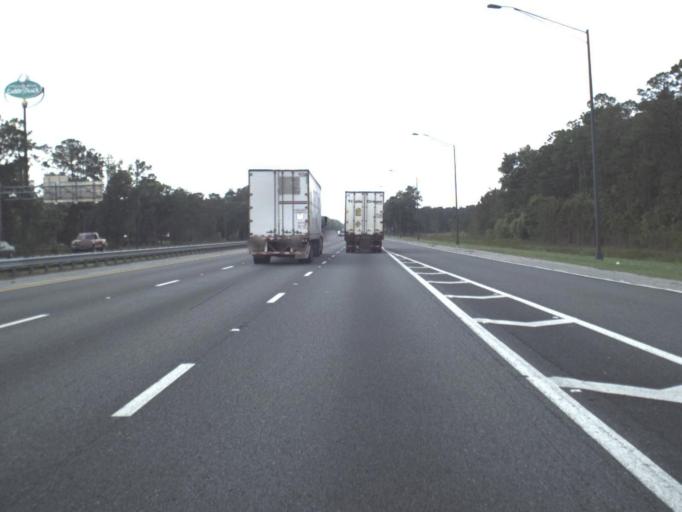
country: US
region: Florida
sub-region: Saint Johns County
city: Villano Beach
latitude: 29.9913
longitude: -81.4648
